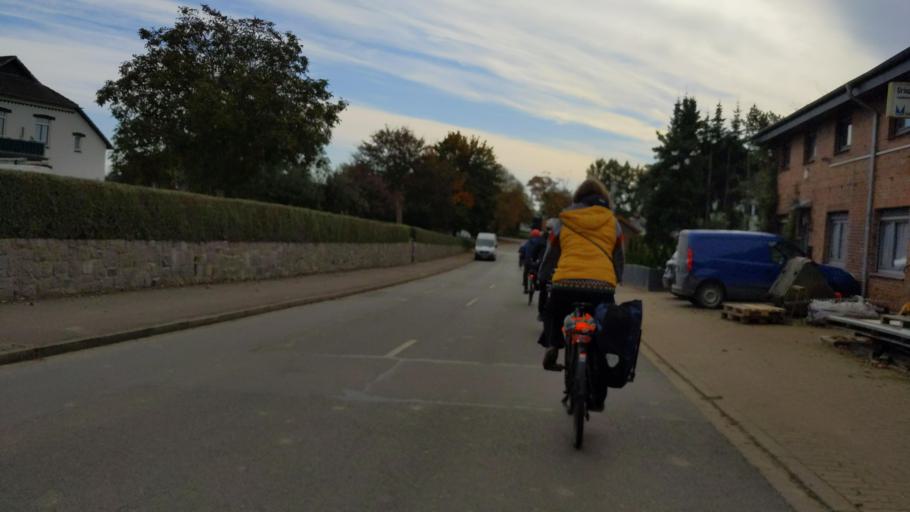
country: DE
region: Schleswig-Holstein
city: Rehhorst
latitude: 53.8745
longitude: 10.4709
